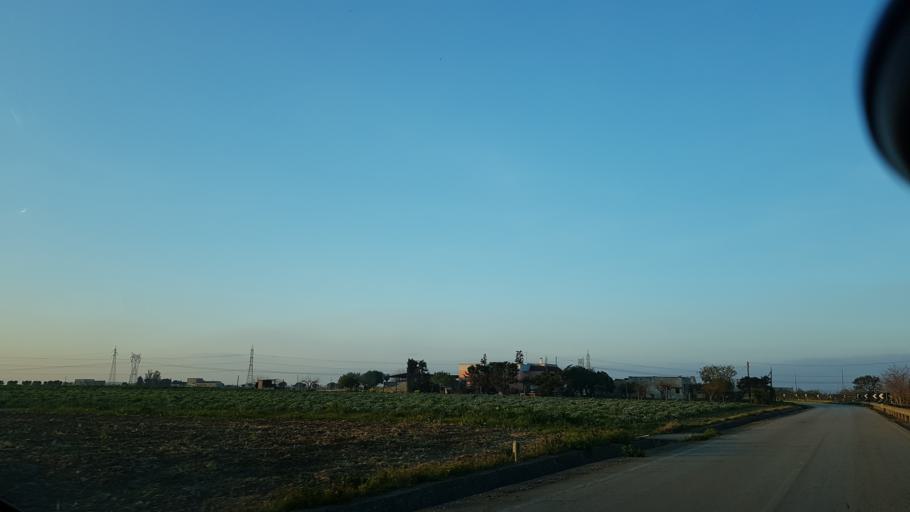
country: IT
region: Apulia
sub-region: Provincia di Brindisi
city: La Rosa
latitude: 40.5956
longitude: 17.9462
